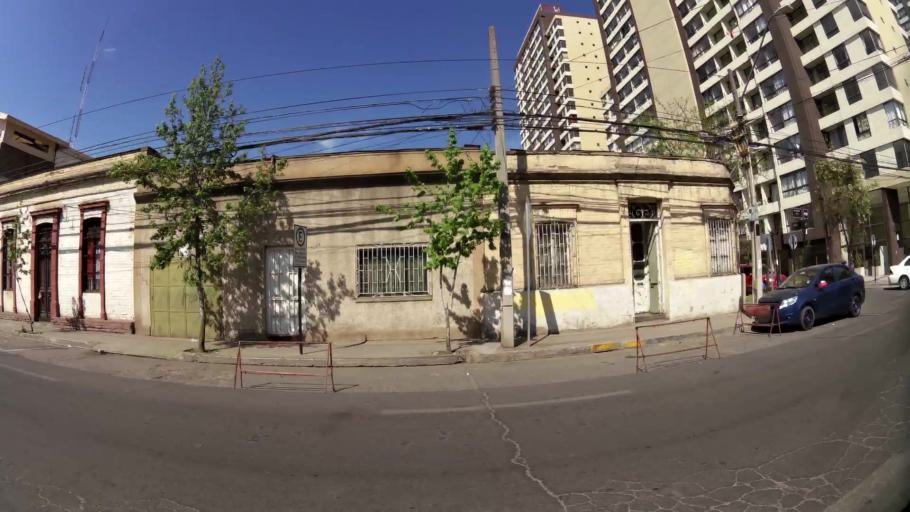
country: CL
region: Santiago Metropolitan
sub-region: Provincia de Santiago
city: Santiago
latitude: -33.4072
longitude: -70.6625
